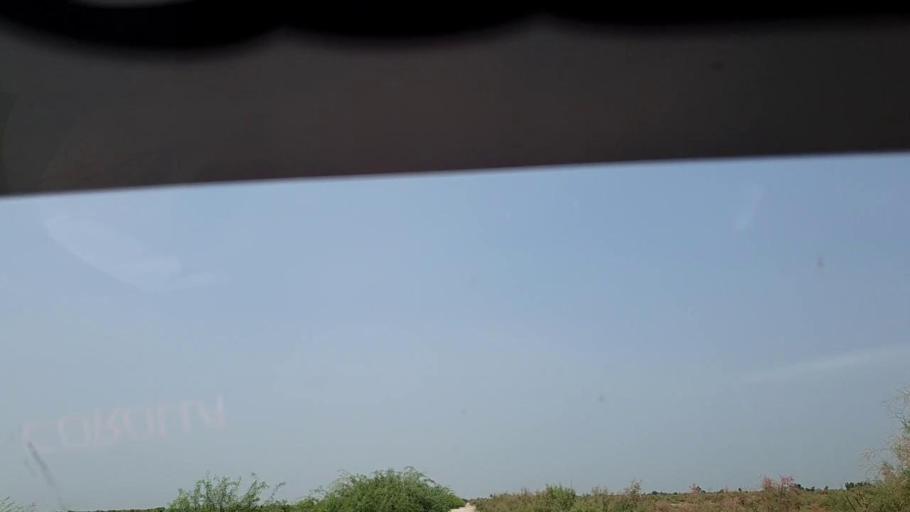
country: PK
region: Sindh
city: Adilpur
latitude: 27.8878
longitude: 69.2559
